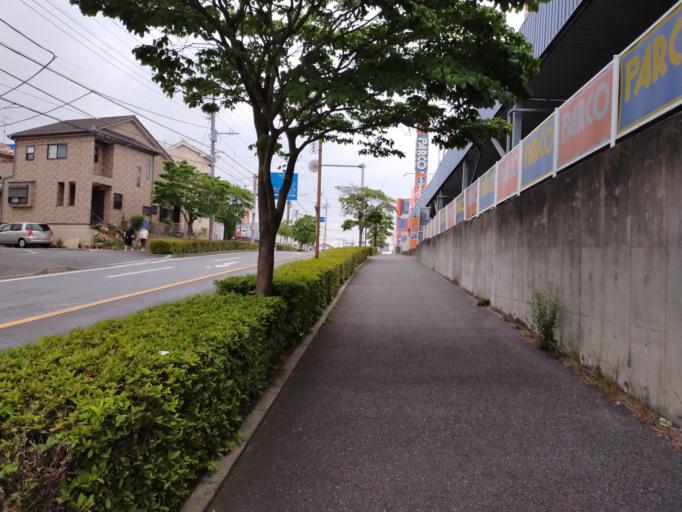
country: JP
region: Chiba
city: Chiba
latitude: 35.6173
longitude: 140.1552
